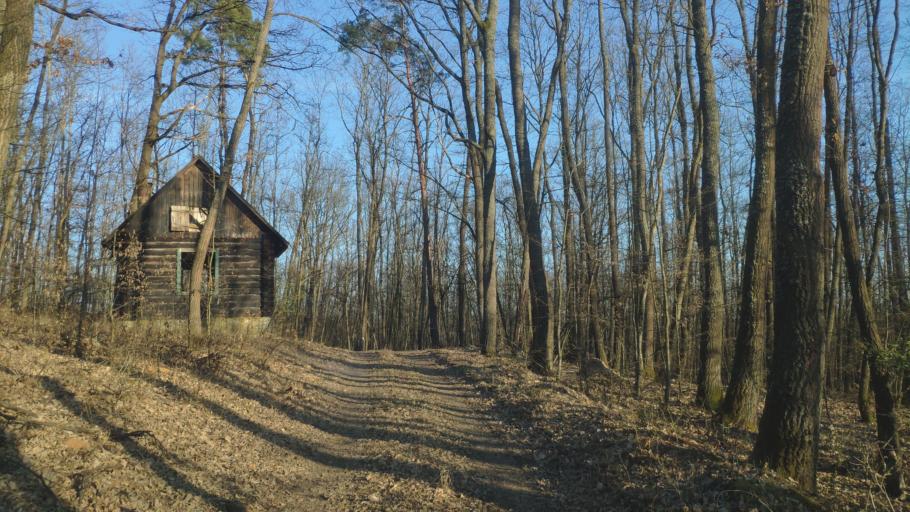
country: HU
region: Borsod-Abauj-Zemplen
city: Putnok
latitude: 48.5051
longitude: 20.3137
